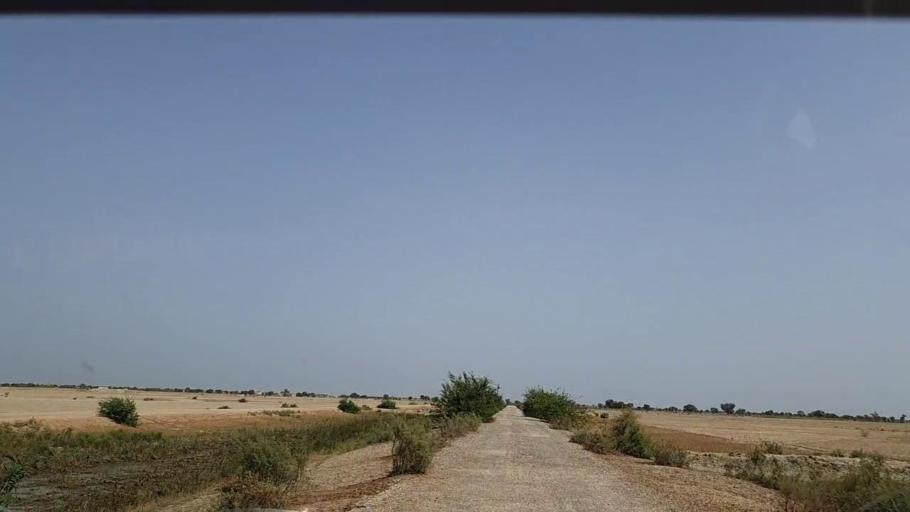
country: PK
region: Sindh
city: Johi
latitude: 26.7597
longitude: 67.6646
